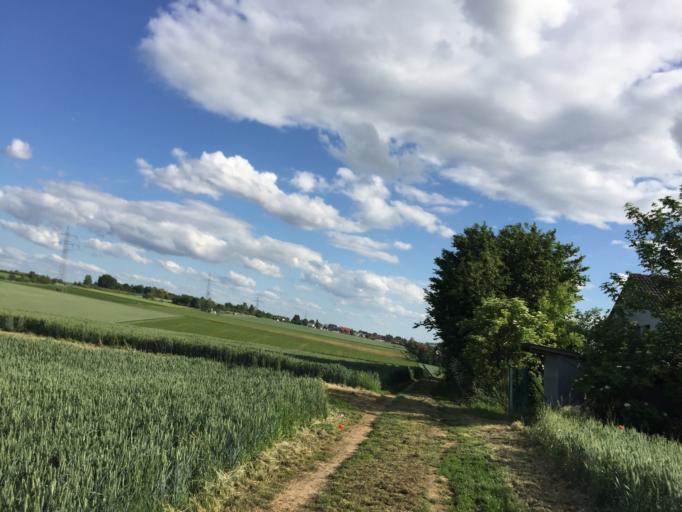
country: DE
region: Hesse
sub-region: Regierungsbezirk Darmstadt
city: Karben
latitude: 50.2322
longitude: 8.7795
